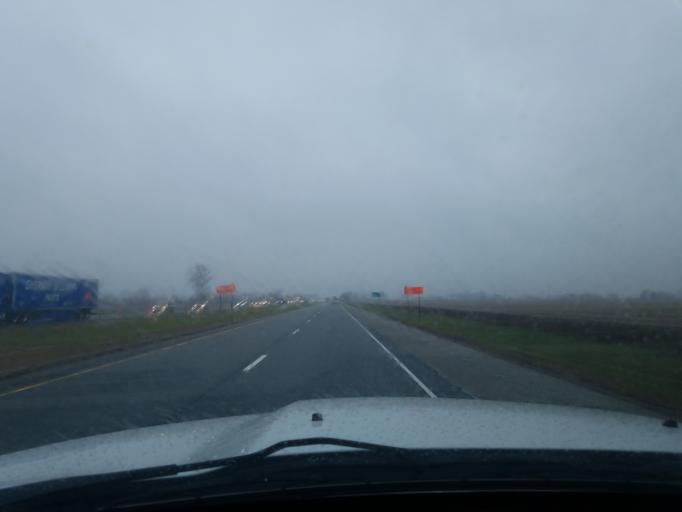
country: US
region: Indiana
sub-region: Grant County
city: Upland
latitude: 40.4148
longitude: -85.5493
